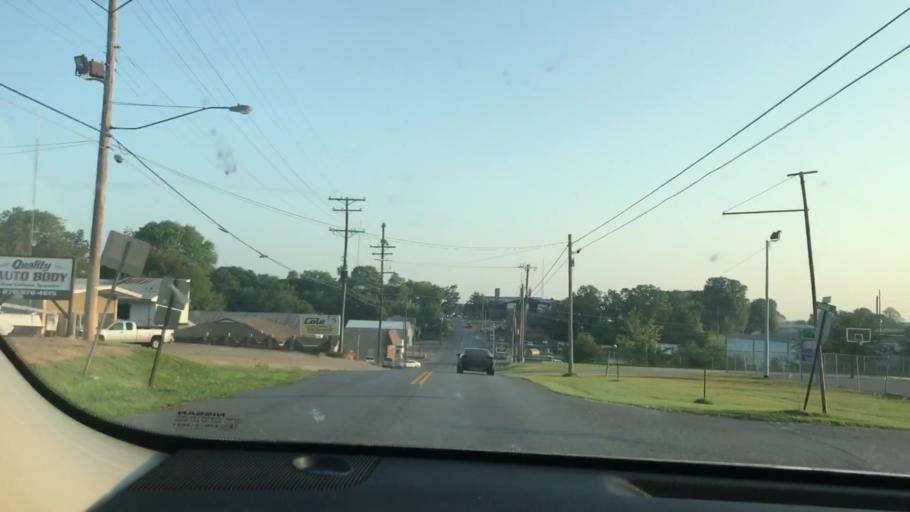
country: US
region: Kentucky
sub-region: Calloway County
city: Murray
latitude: 36.6044
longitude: -88.3023
